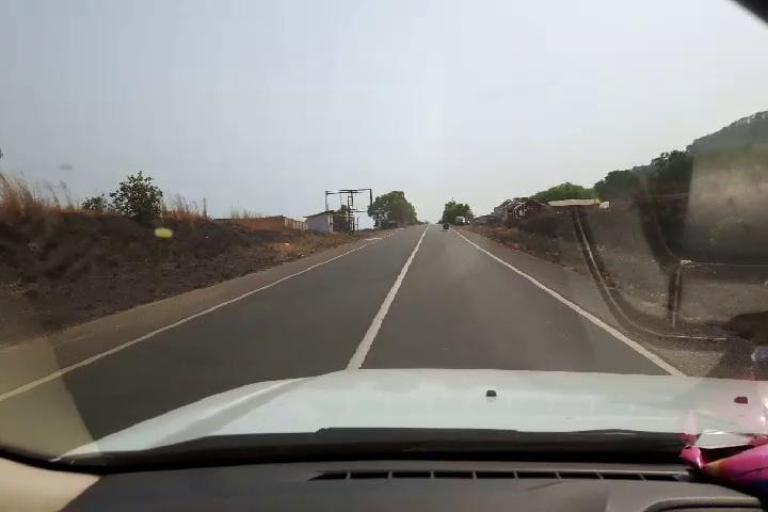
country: SL
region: Western Area
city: Waterloo
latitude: 8.2057
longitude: -13.1095
